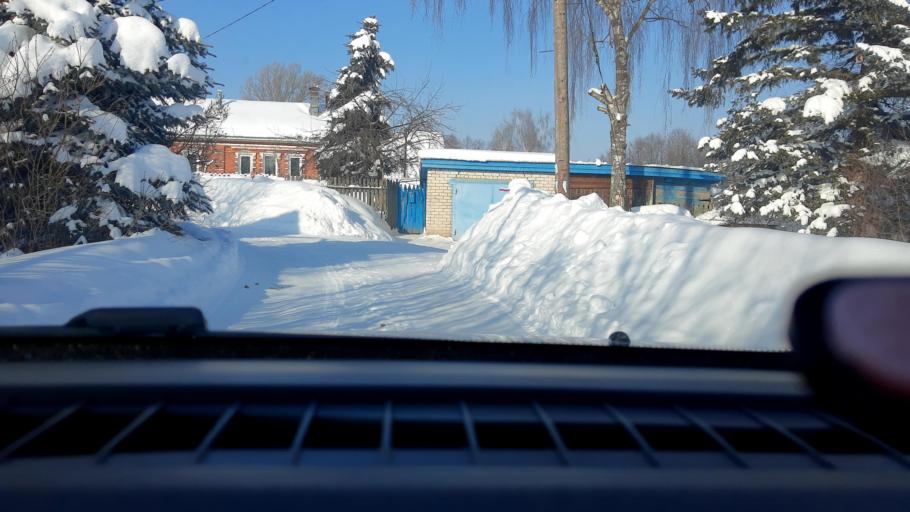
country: RU
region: Nizjnij Novgorod
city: Afonino
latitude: 56.1958
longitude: 44.0520
